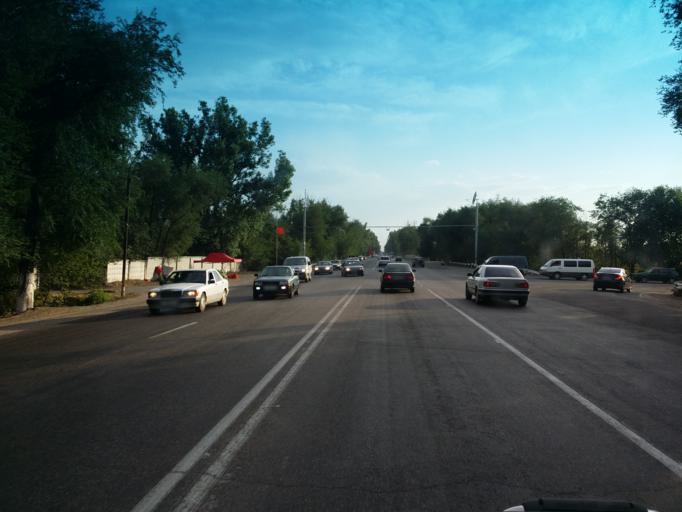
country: KZ
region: Almaty Oblysy
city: Energeticheskiy
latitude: 43.3670
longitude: 77.0875
